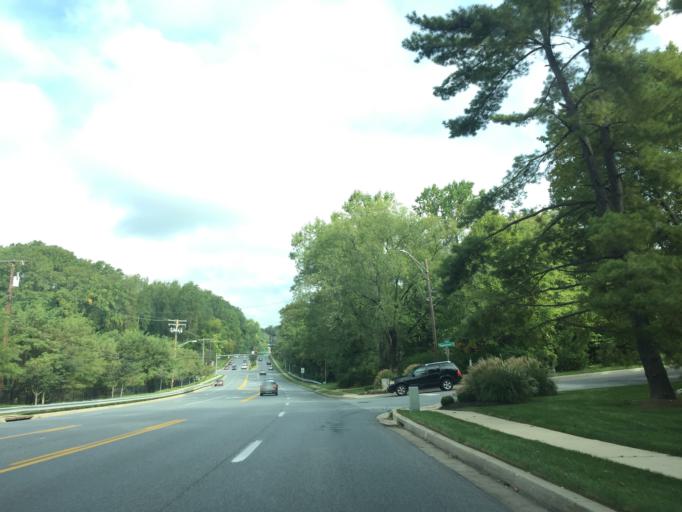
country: US
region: Maryland
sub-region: Baltimore County
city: Pikesville
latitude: 39.3838
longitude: -76.6852
